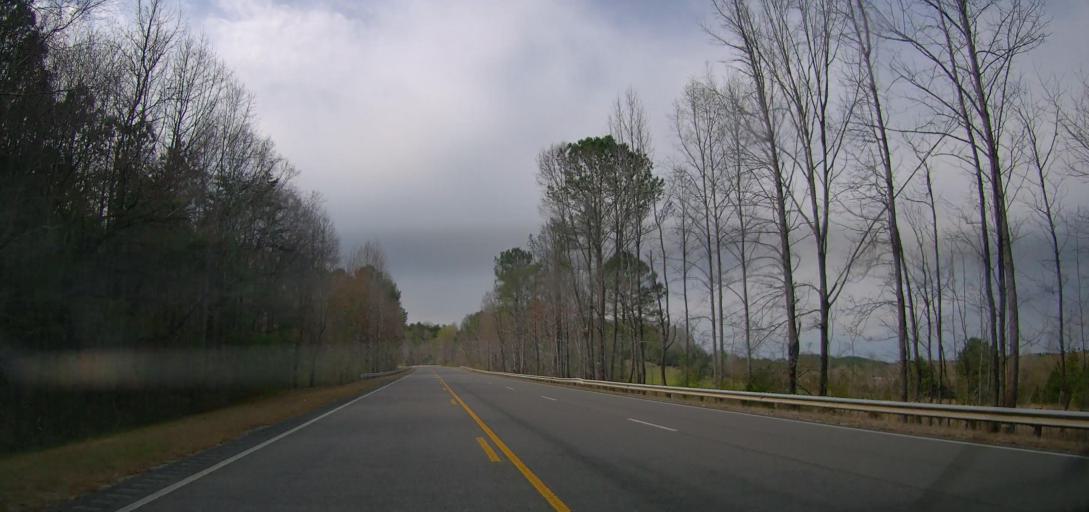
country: US
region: Alabama
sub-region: Walker County
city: Carbon Hill
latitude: 33.9143
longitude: -87.5640
